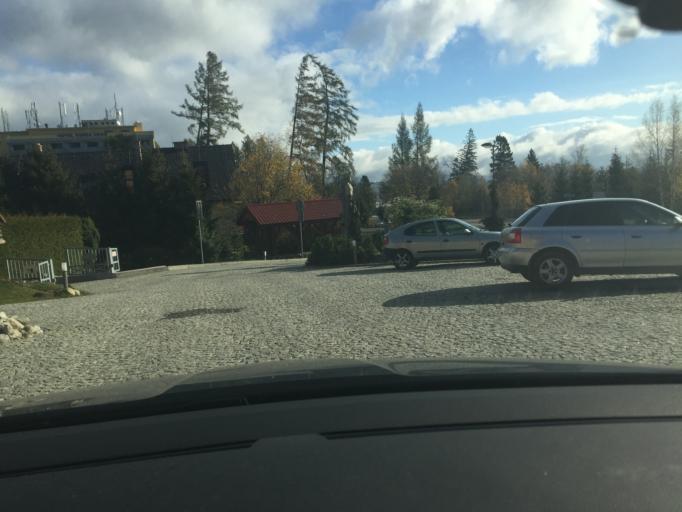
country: SK
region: Presovsky
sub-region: Okres Poprad
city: Vysoke Tatry
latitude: 49.1634
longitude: 20.2734
